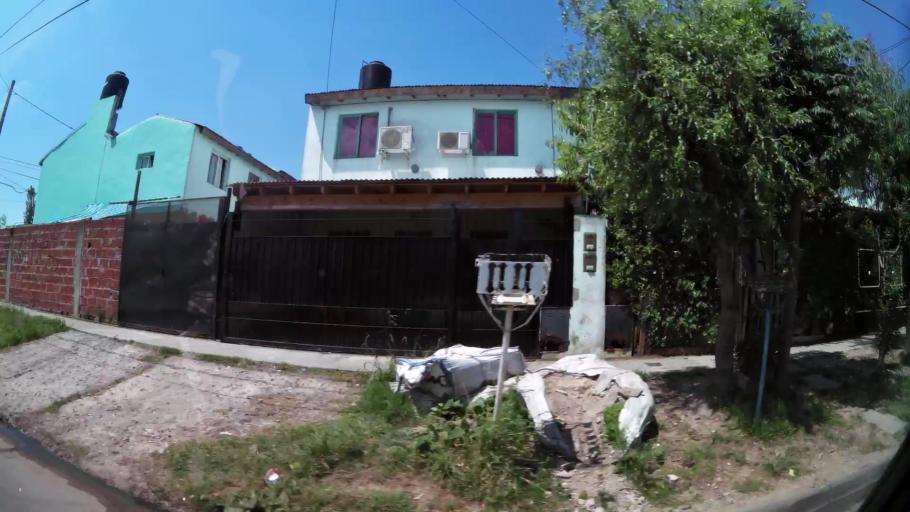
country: AR
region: Buenos Aires
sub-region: Partido de Tigre
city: Tigre
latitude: -34.4582
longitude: -58.5831
